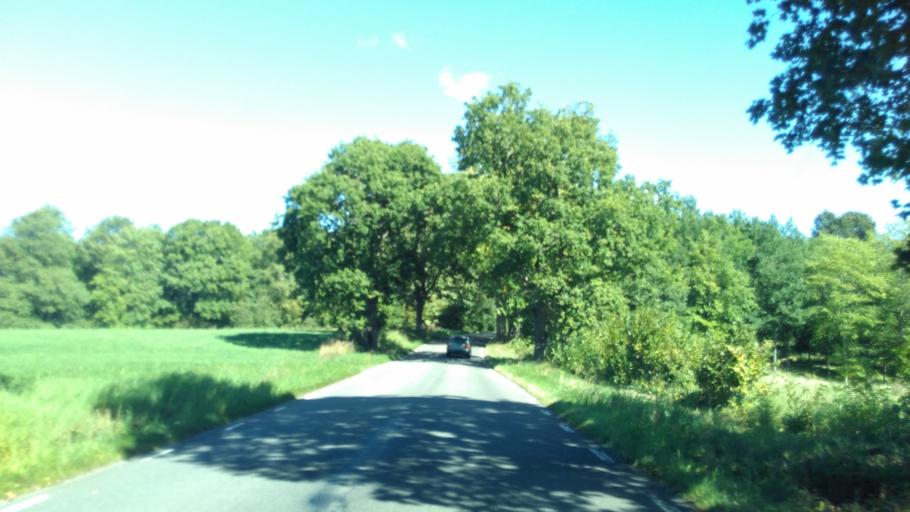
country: SE
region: Vaestra Goetaland
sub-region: Skara Kommun
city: Axvall
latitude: 58.4439
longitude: 13.6607
